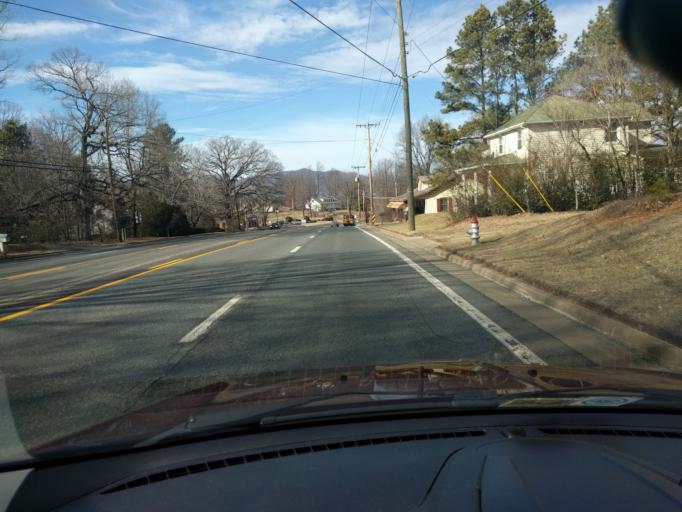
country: US
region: Virginia
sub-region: Amherst County
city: Madison Heights
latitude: 37.4889
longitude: -79.1232
